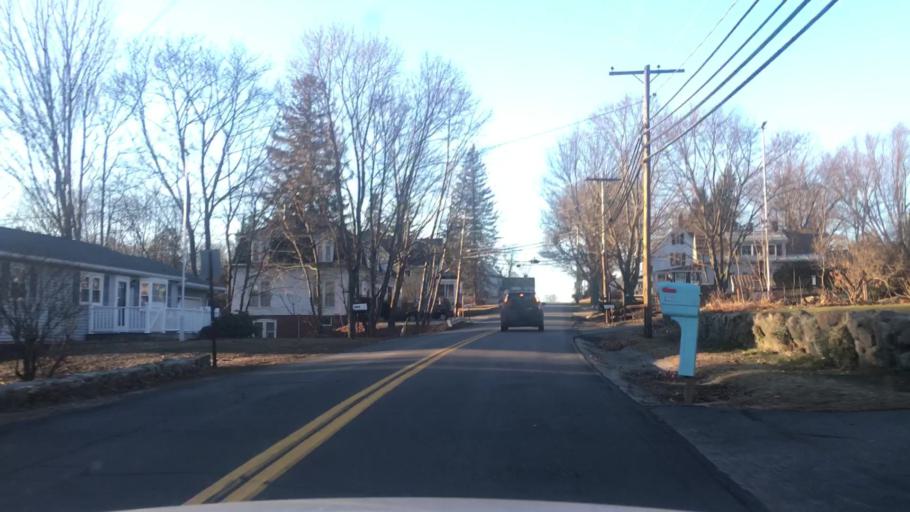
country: US
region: Maine
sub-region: York County
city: South Eliot
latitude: 43.1107
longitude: -70.7744
